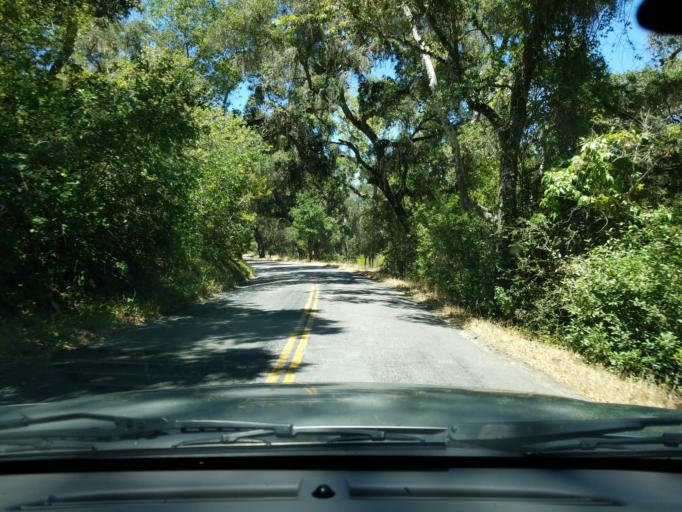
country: US
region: California
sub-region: Monterey County
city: Chualar
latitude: 36.4154
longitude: -121.5979
